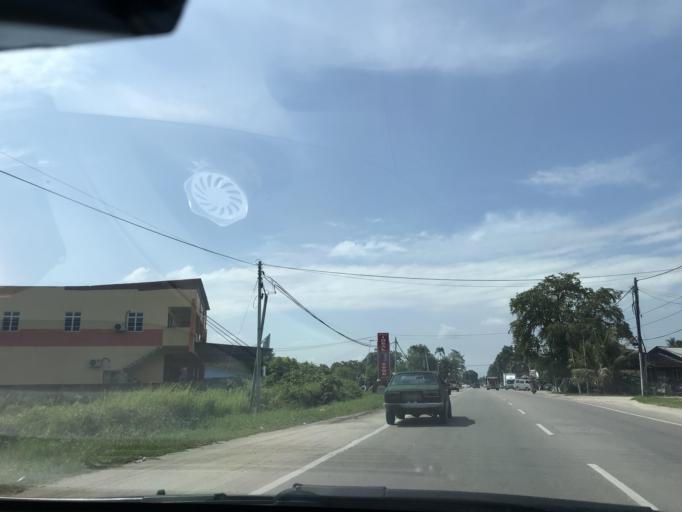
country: MY
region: Kelantan
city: Tumpat
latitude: 6.1481
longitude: 102.1624
